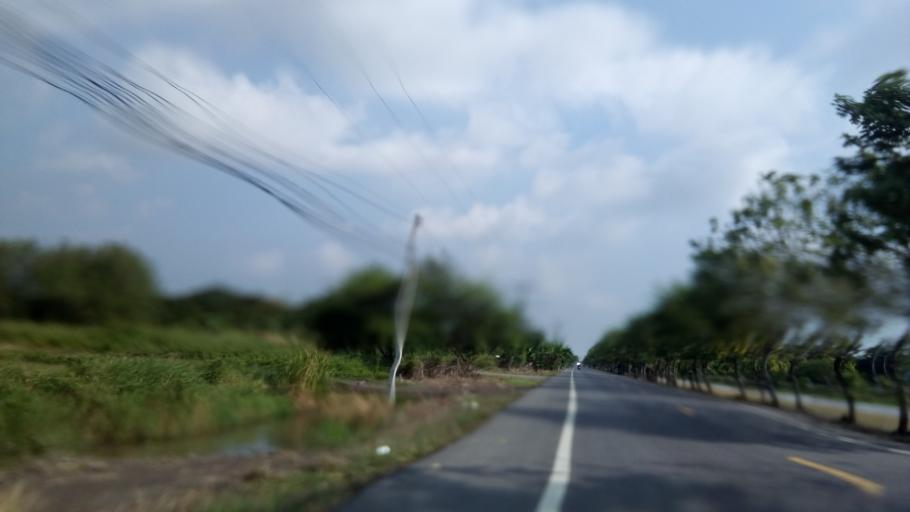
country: TH
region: Pathum Thani
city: Nong Suea
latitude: 14.1606
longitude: 100.8459
